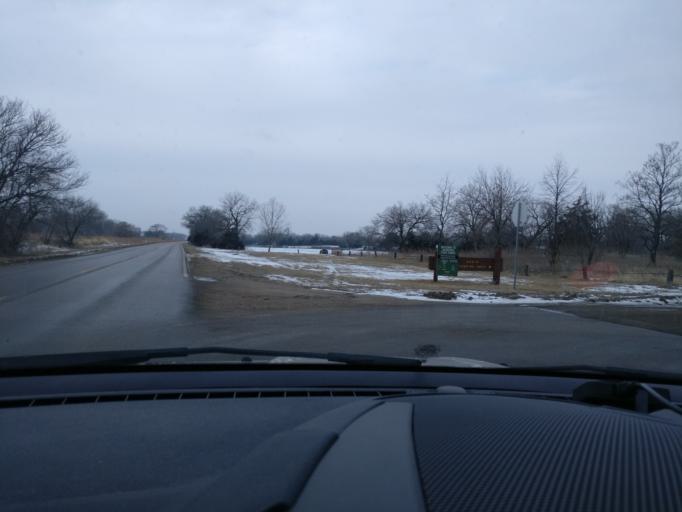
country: US
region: Nebraska
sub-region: Dodge County
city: Fremont
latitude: 41.4485
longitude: -96.5684
